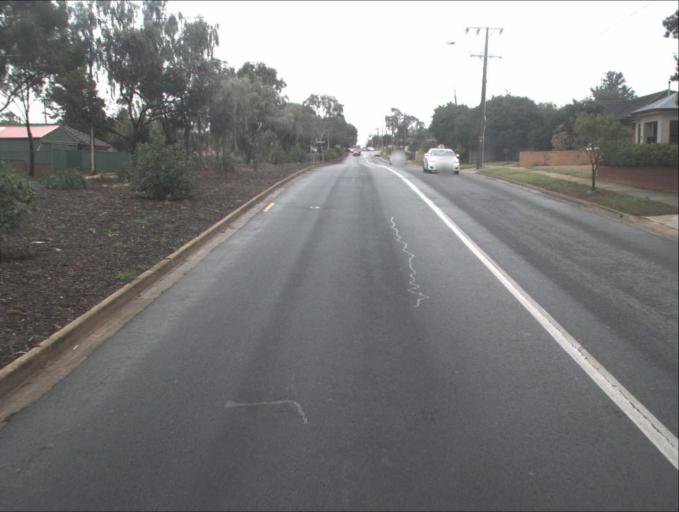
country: AU
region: South Australia
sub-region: Port Adelaide Enfield
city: Gilles Plains
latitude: -34.8380
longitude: 138.6625
